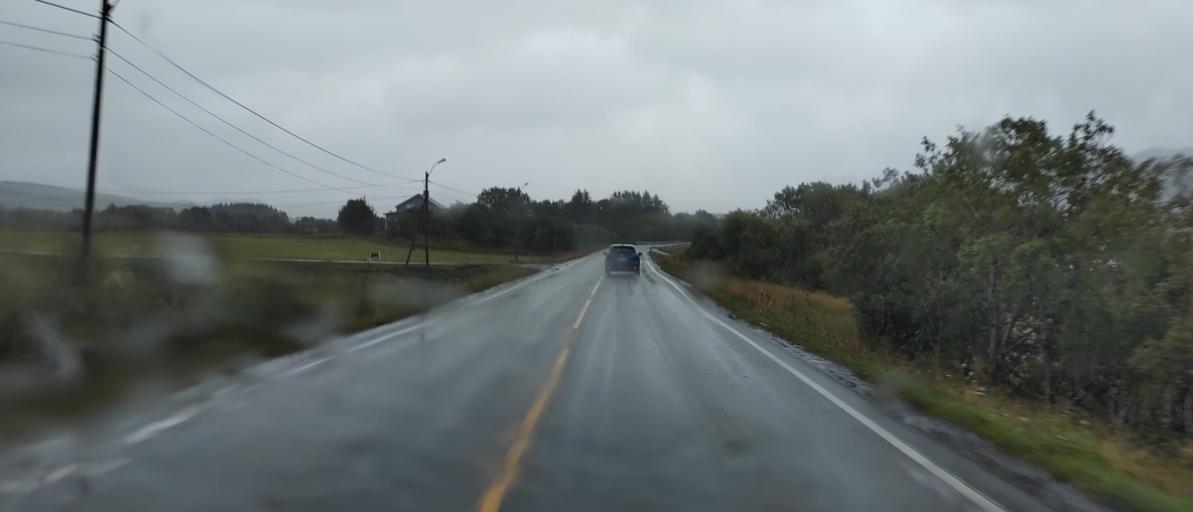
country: NO
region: Nordland
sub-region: Vestvagoy
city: Evjen
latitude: 68.2120
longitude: 13.7061
